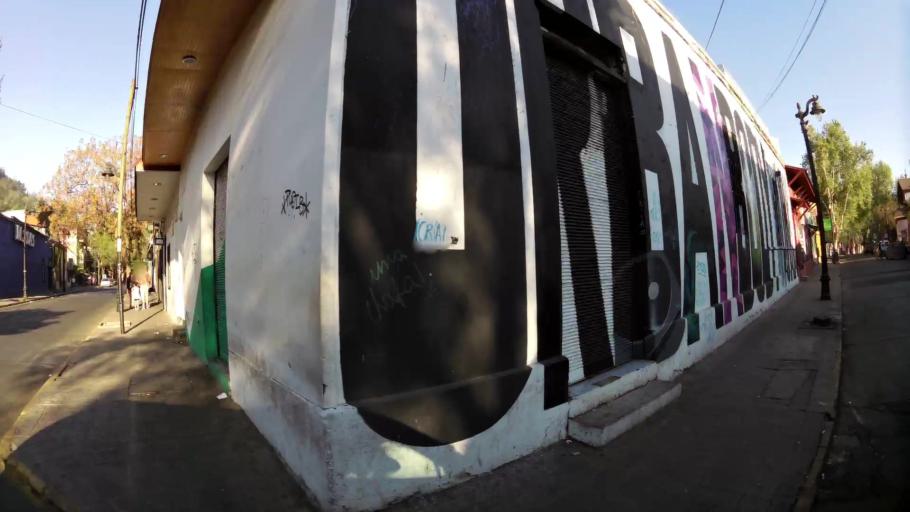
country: CL
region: Santiago Metropolitan
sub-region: Provincia de Santiago
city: Santiago
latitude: -33.4305
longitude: -70.6396
